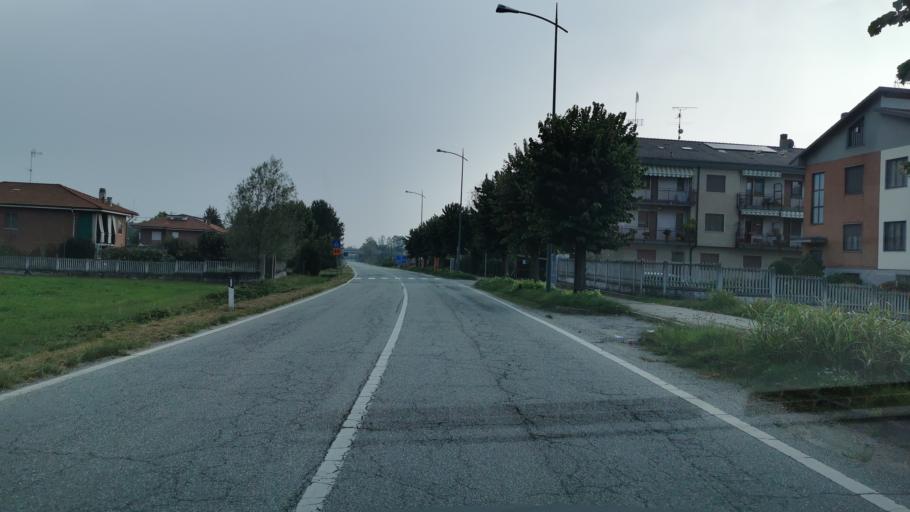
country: IT
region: Piedmont
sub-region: Provincia di Torino
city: Lombardore
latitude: 45.2326
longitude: 7.7428
